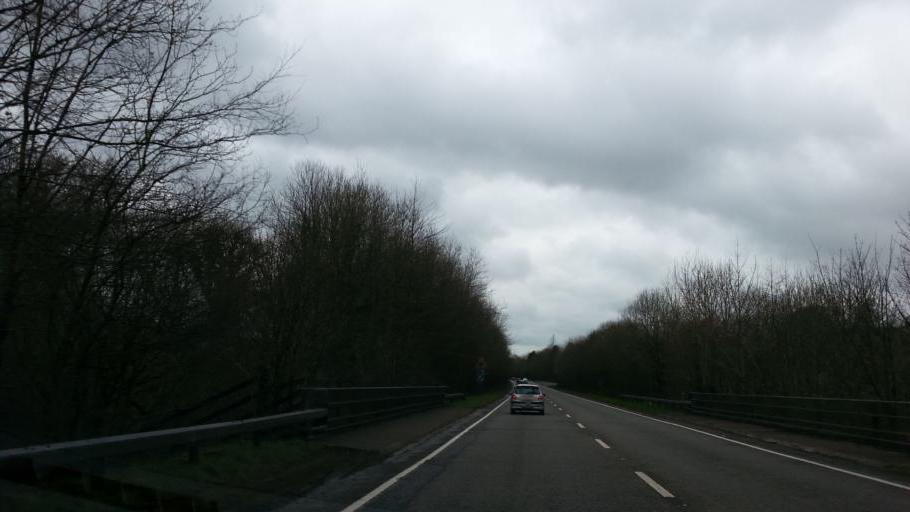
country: GB
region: England
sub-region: Devon
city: South Molton
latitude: 51.0481
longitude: -3.8958
